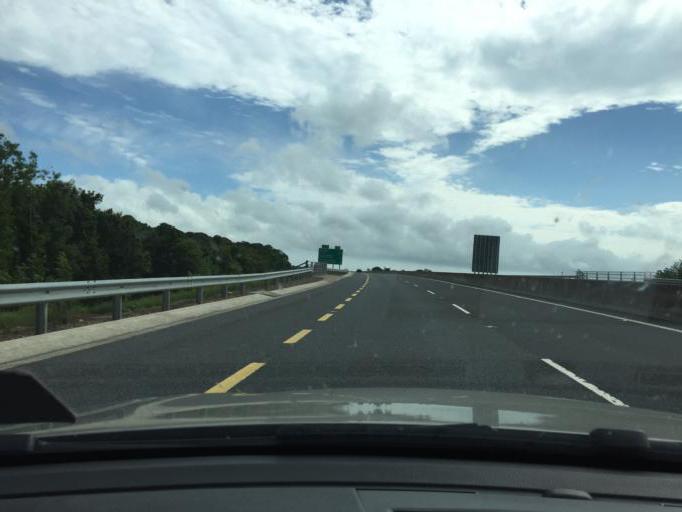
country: IE
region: Leinster
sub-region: Kilkenny
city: Mooncoin
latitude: 52.2530
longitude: -7.1903
